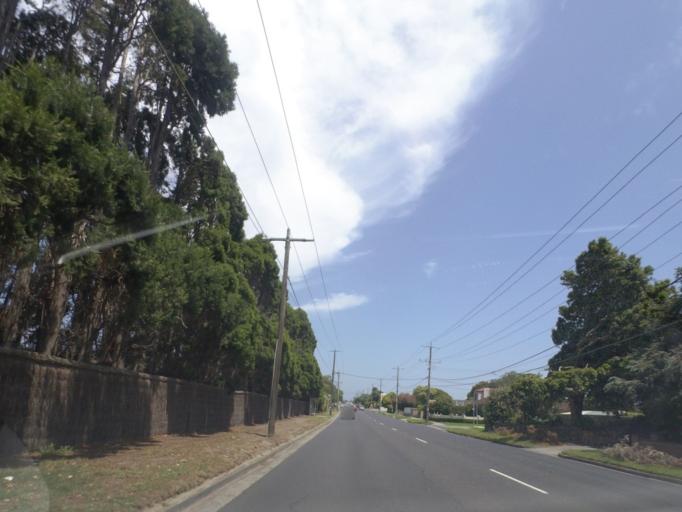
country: AU
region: Victoria
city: Heatherton
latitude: -37.9544
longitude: 145.0870
